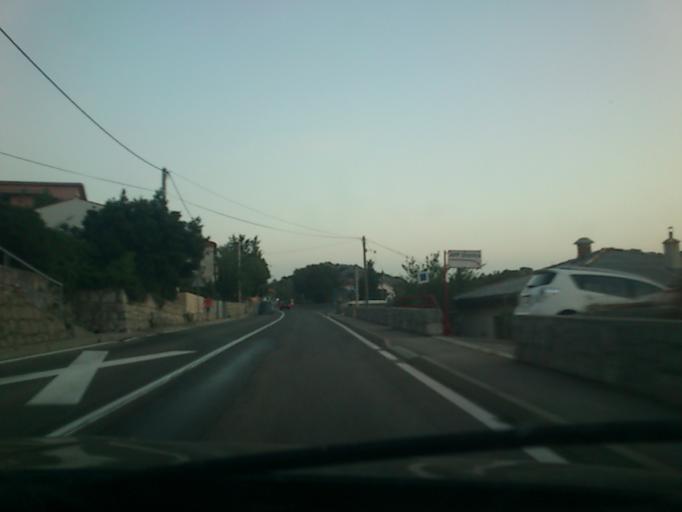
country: HR
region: Licko-Senjska
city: Senj
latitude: 44.9291
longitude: 14.9213
